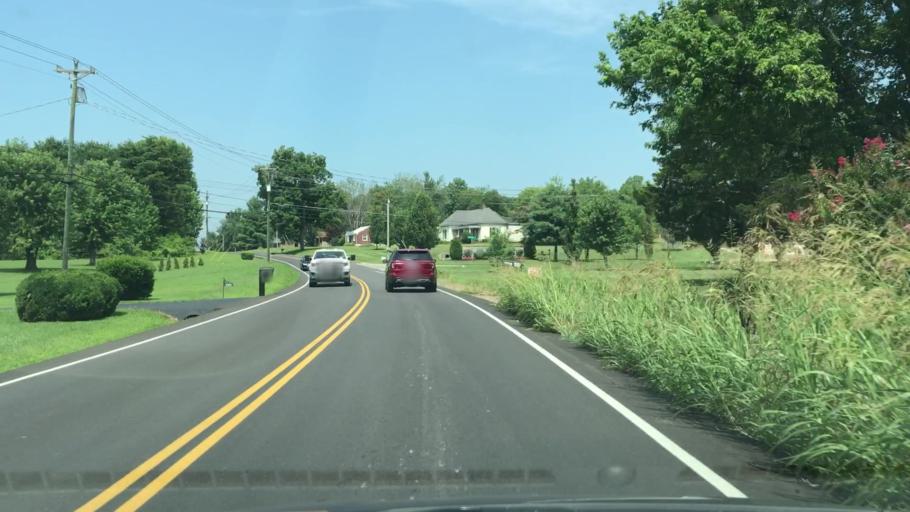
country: US
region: Tennessee
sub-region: Wilson County
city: Rural Hill
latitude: 36.1154
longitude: -86.4593
